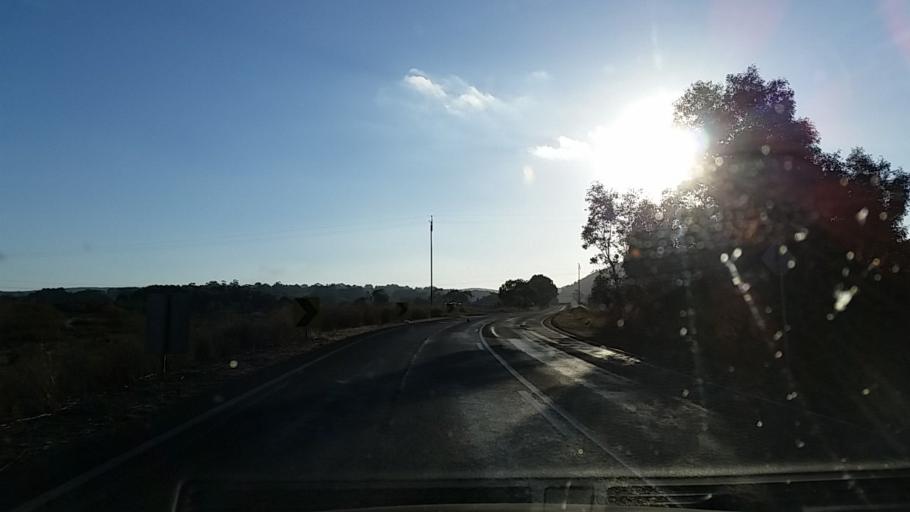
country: AU
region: South Australia
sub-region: Alexandrina
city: Mount Compass
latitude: -35.3495
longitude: 138.6335
